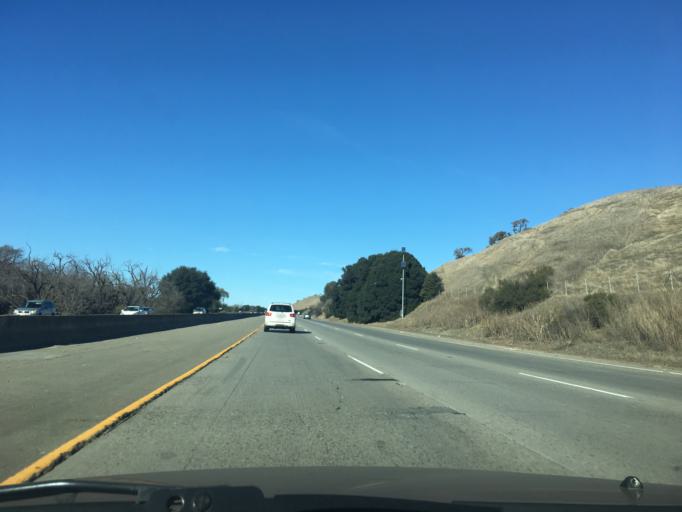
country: US
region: California
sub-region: Alameda County
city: Pleasanton
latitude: 37.6048
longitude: -121.8721
